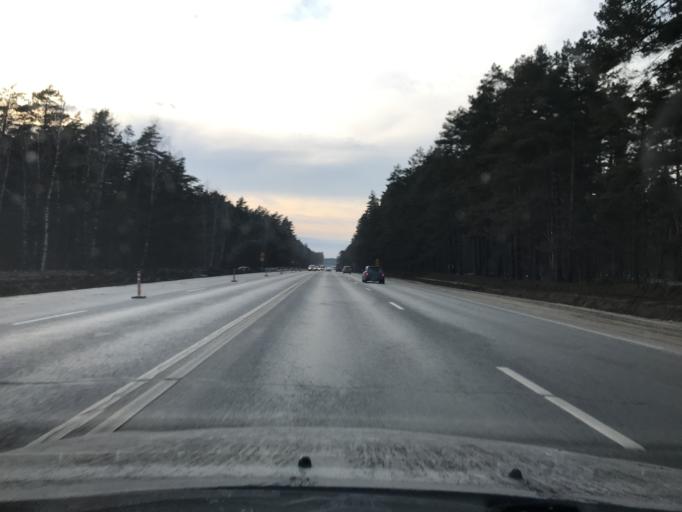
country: RU
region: Kaluga
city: Mstikhino
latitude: 54.5780
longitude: 36.0970
